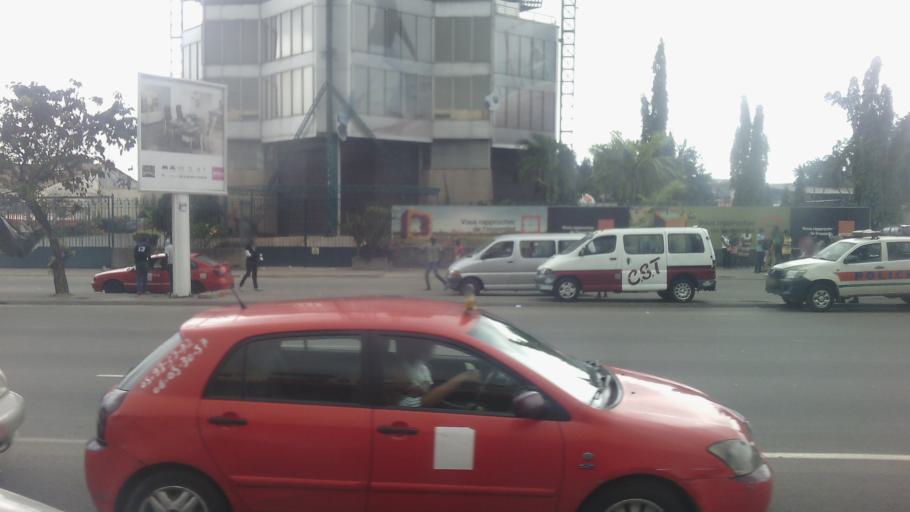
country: CI
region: Lagunes
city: Abidjan
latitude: 5.2980
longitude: -3.9848
